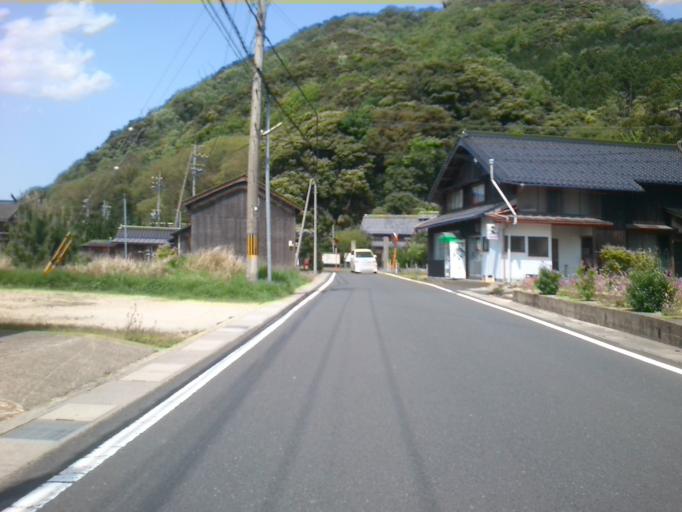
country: JP
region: Kyoto
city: Miyazu
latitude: 35.7364
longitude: 135.1107
